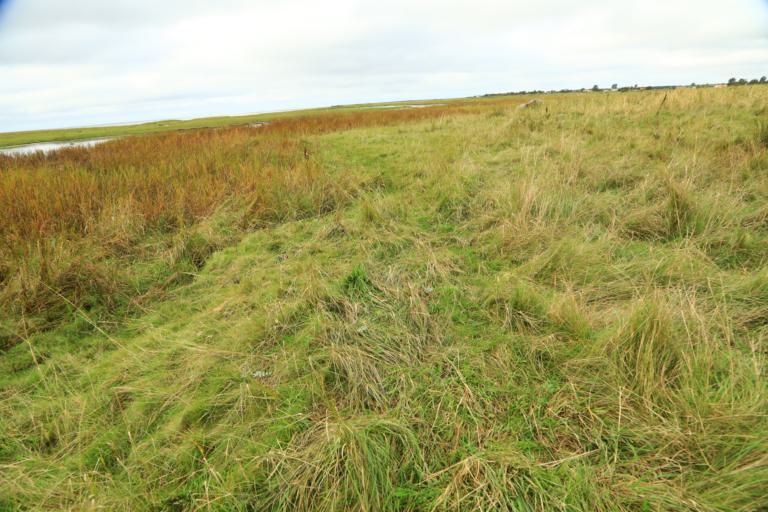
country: SE
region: Halland
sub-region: Varbergs Kommun
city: Tvaaker
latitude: 57.0186
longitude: 12.3393
